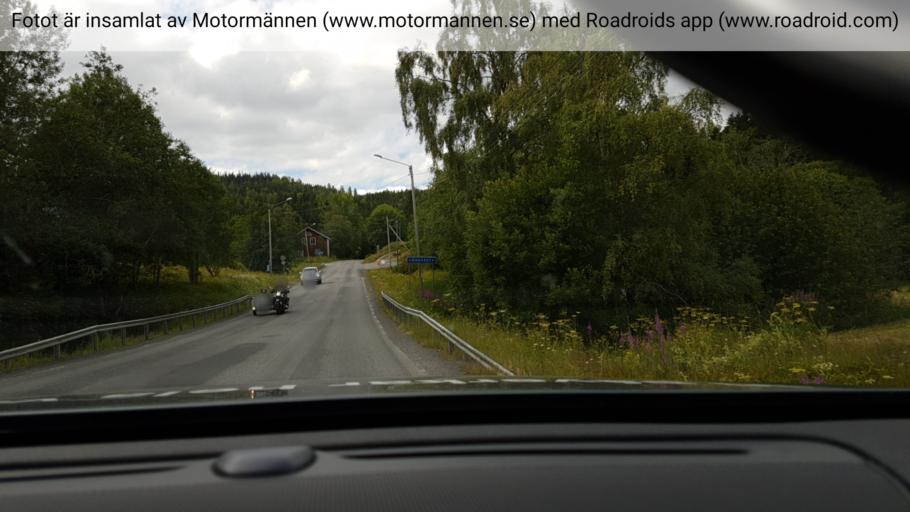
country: SE
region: Vaesternorrland
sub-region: Kramfors Kommun
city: Nordingra
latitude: 62.9364
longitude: 18.2369
